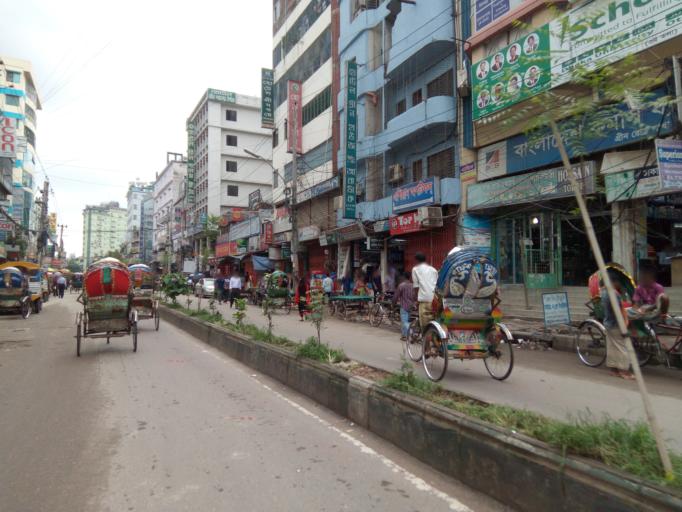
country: BD
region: Dhaka
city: Azimpur
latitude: 23.7553
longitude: 90.3891
